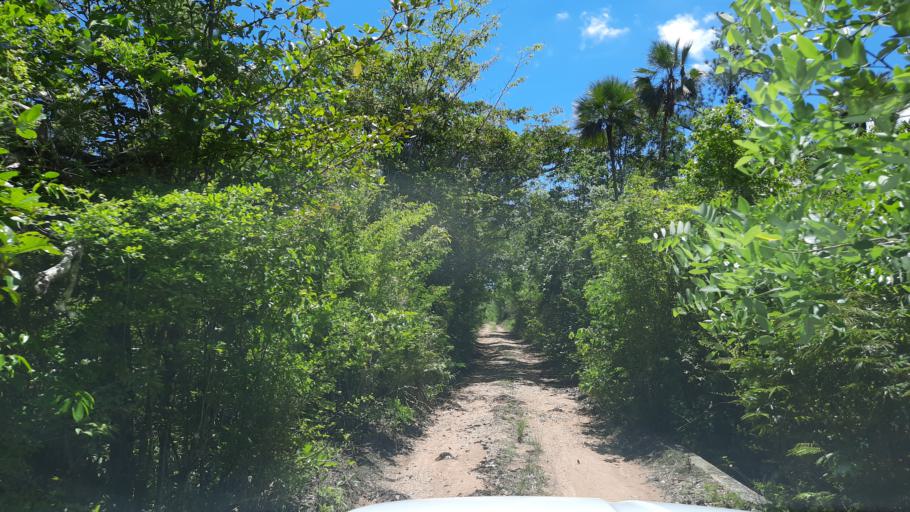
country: BZ
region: Cayo
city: Belmopan
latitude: 17.3566
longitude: -88.5393
